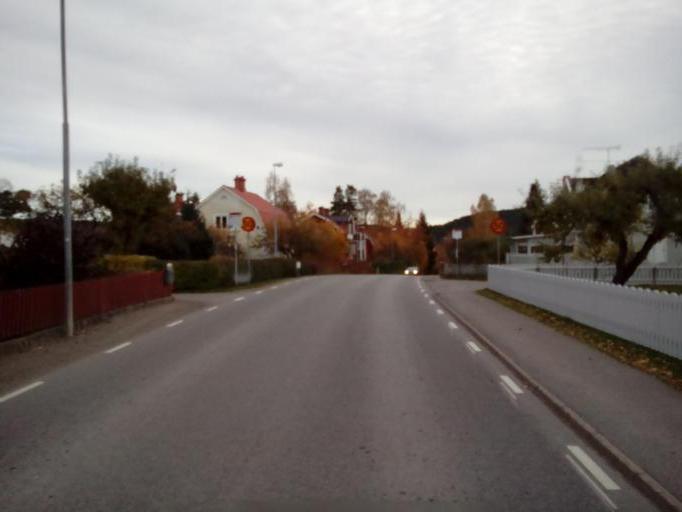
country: SE
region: OEstergoetland
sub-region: Kinda Kommun
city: Kisa
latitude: 57.9872
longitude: 15.6445
